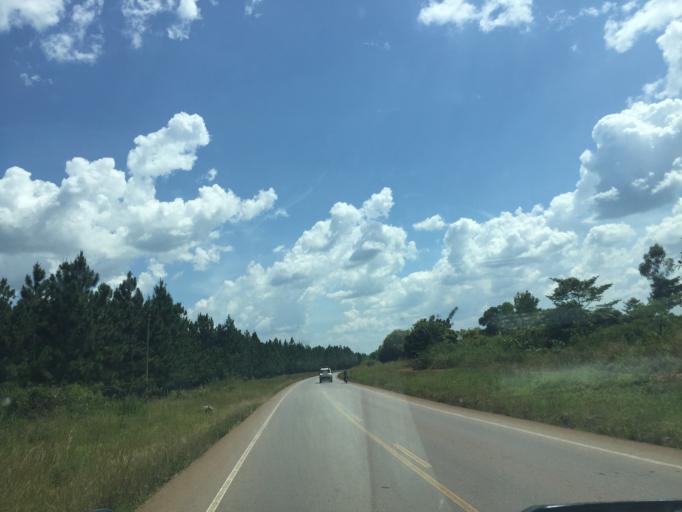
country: UG
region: Central Region
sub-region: Nakasongola District
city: Nakasongola
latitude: 1.2225
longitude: 32.4653
